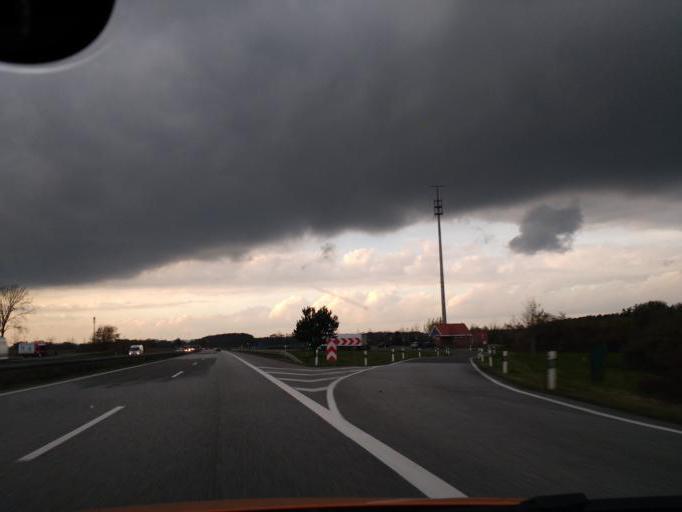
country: DE
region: Brandenburg
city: Gerdshagen
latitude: 53.2633
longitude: 12.1458
